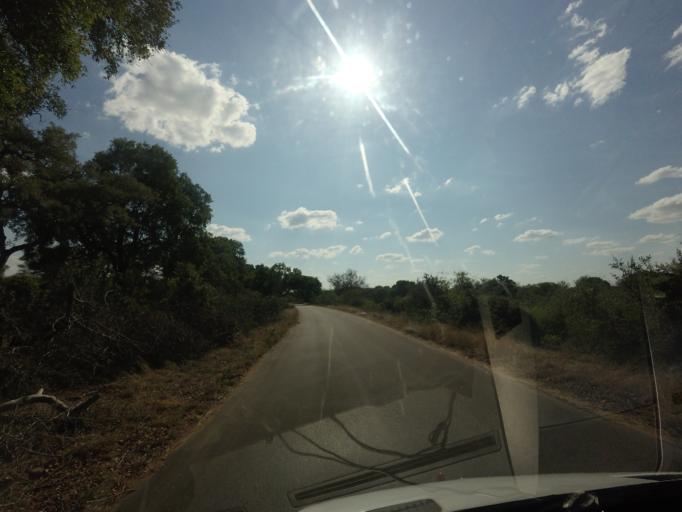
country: ZA
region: Limpopo
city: Thulamahashi
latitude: -24.4156
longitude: 31.5178
